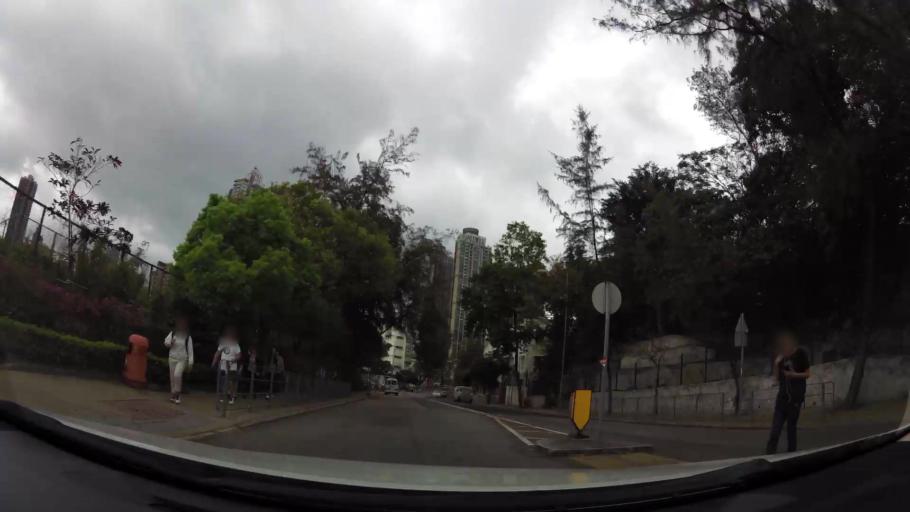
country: HK
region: Kowloon City
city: Kowloon
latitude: 22.3231
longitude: 114.1842
